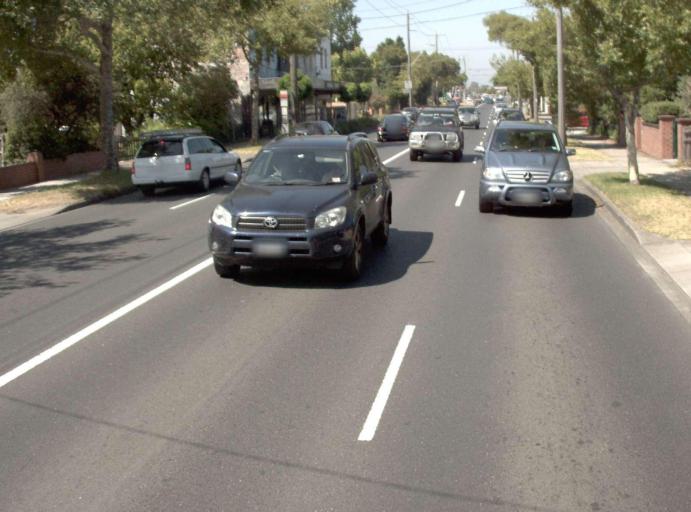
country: AU
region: Victoria
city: Hughesdale
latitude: -37.9059
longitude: 145.0857
